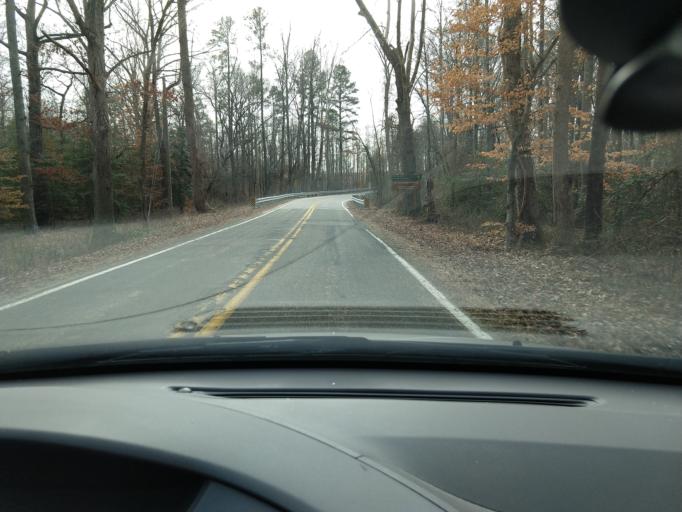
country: US
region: Virginia
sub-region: Henrico County
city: Fort Lee
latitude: 37.4202
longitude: -77.2450
